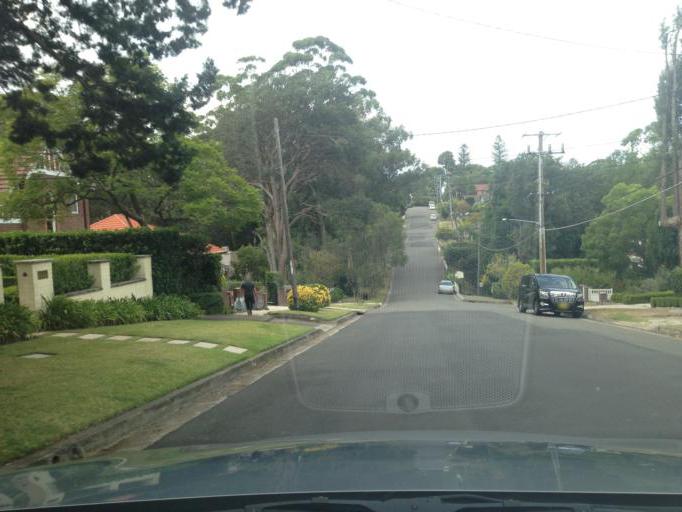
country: AU
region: New South Wales
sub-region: Ku-ring-gai
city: Killara
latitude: -33.7665
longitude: 151.1701
